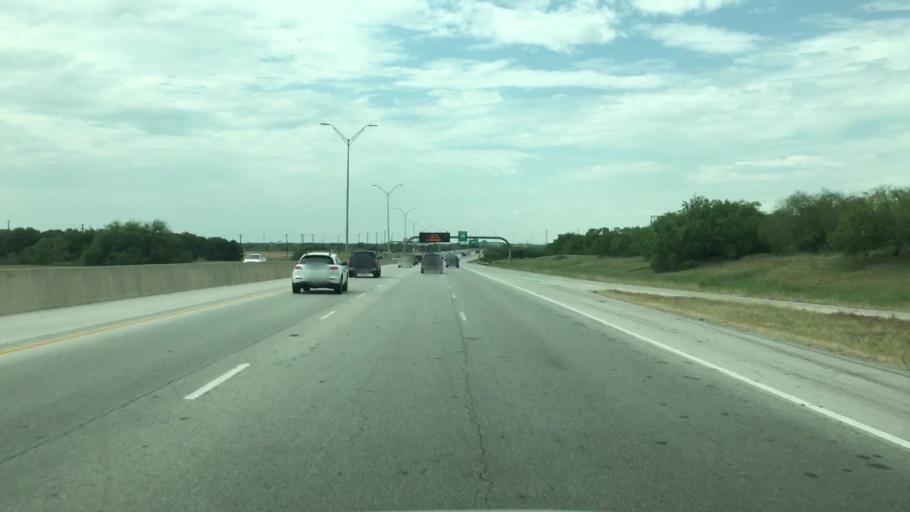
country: US
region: Texas
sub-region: Bexar County
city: Elmendorf
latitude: 29.3095
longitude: -98.4011
